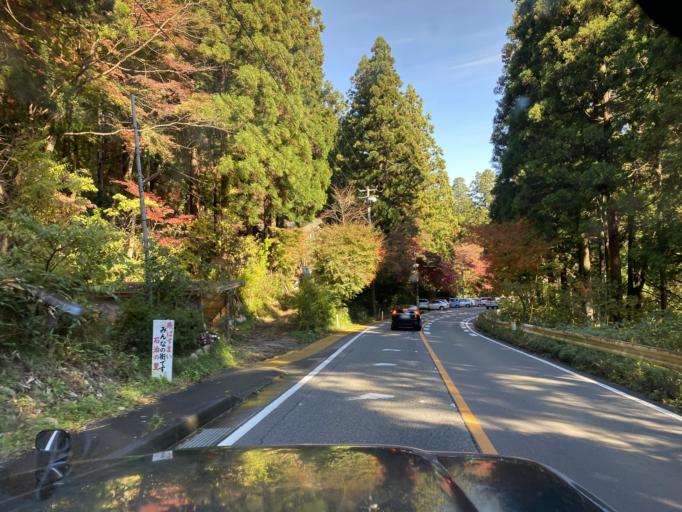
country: JP
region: Niigata
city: Niitsu-honcho
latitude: 37.7496
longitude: 139.1110
